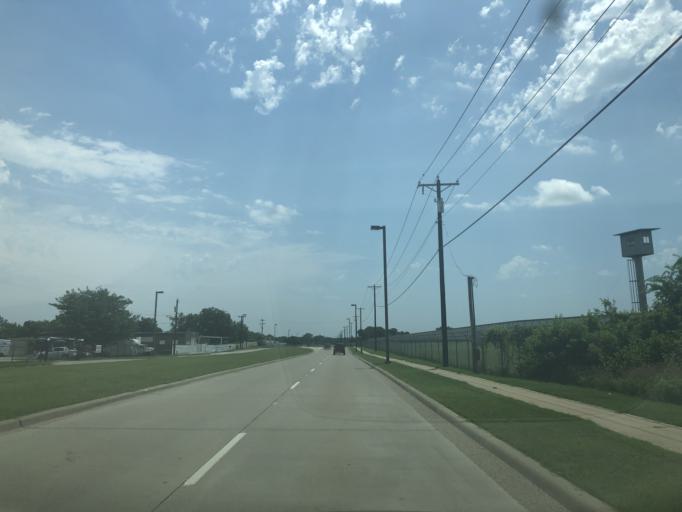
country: US
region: Texas
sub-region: Dallas County
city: Grand Prairie
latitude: 32.7777
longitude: -96.9918
